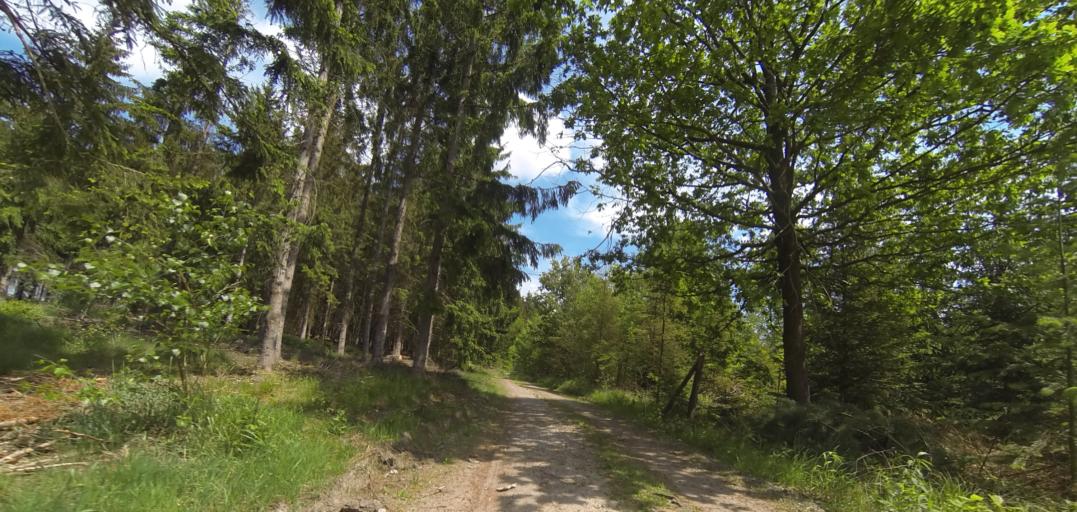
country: DE
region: Saxony
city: Grossharthau
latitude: 51.1077
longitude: 14.1221
